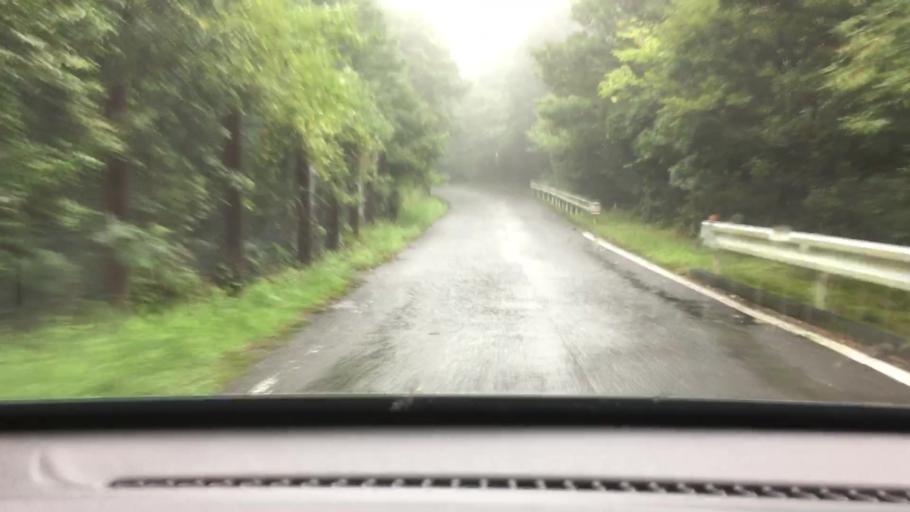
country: JP
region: Nagasaki
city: Togitsu
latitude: 32.9166
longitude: 129.7355
